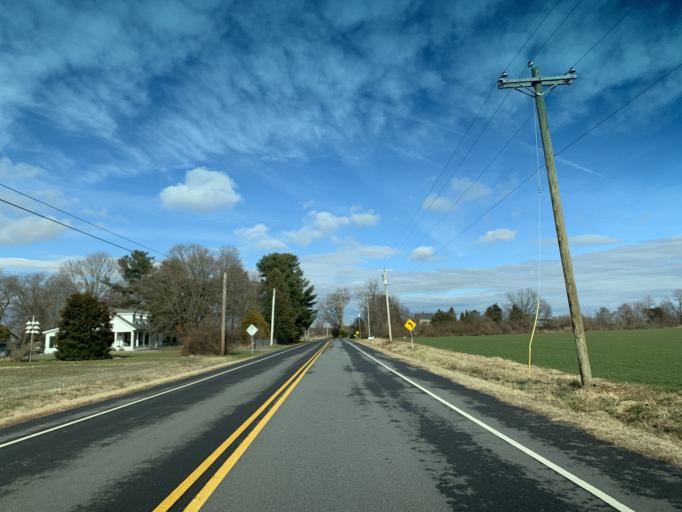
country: US
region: Maryland
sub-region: Kent County
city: Chestertown
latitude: 39.3460
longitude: -76.0622
